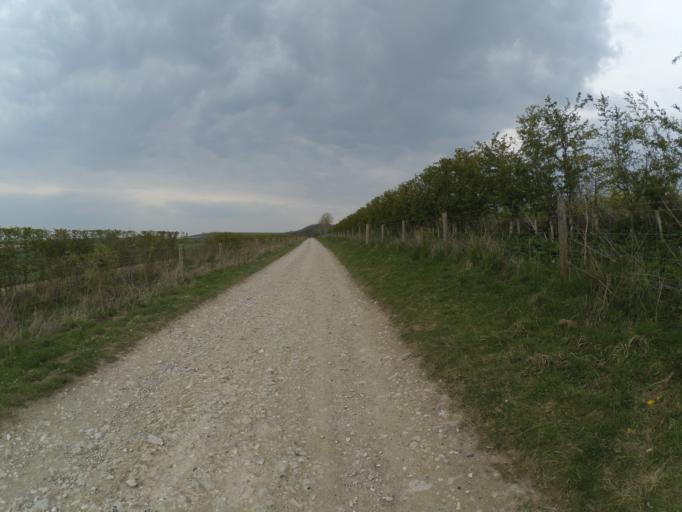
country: GB
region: England
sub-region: West Sussex
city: Arundel
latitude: 50.8843
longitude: -0.5201
